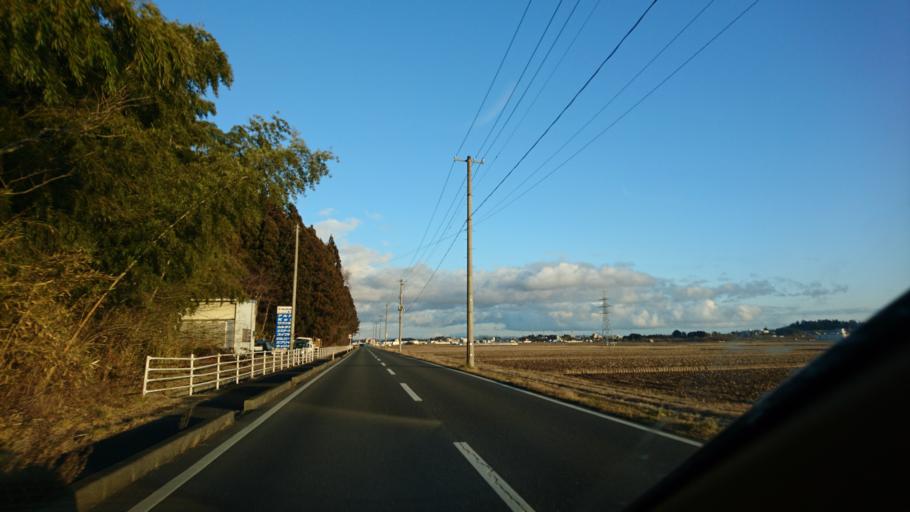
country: JP
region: Miyagi
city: Furukawa
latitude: 38.7473
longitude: 140.9937
